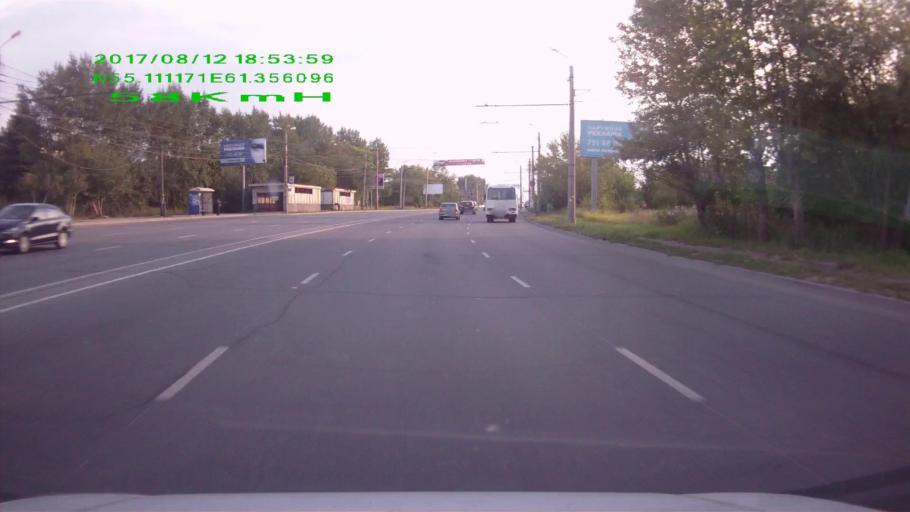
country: RU
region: Chelyabinsk
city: Novosineglazovskiy
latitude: 55.1086
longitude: 61.3525
